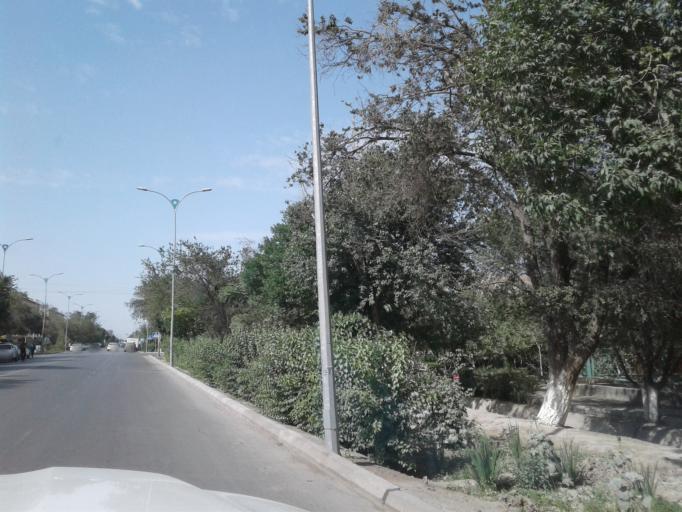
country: TM
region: Dasoguz
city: Dasoguz
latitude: 41.8311
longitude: 59.9456
